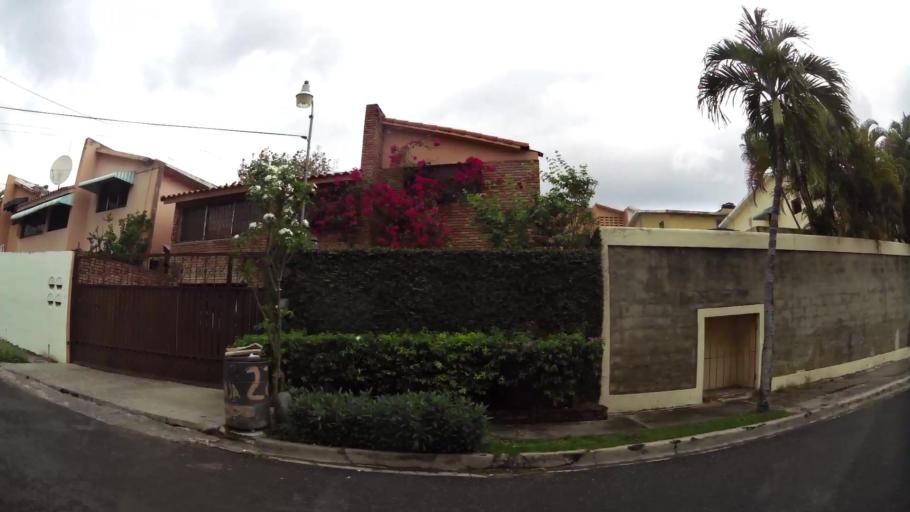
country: DO
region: Nacional
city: La Agustina
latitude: 18.5047
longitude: -69.9366
